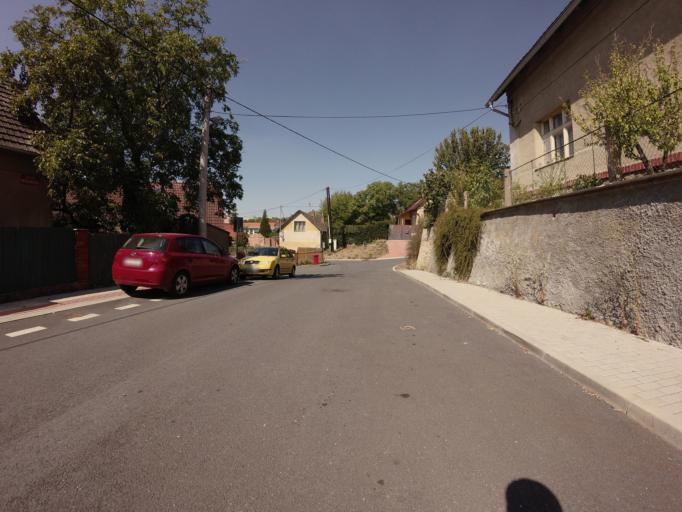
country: CZ
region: Central Bohemia
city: Jilove u Prahy
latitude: 49.8976
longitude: 14.4879
